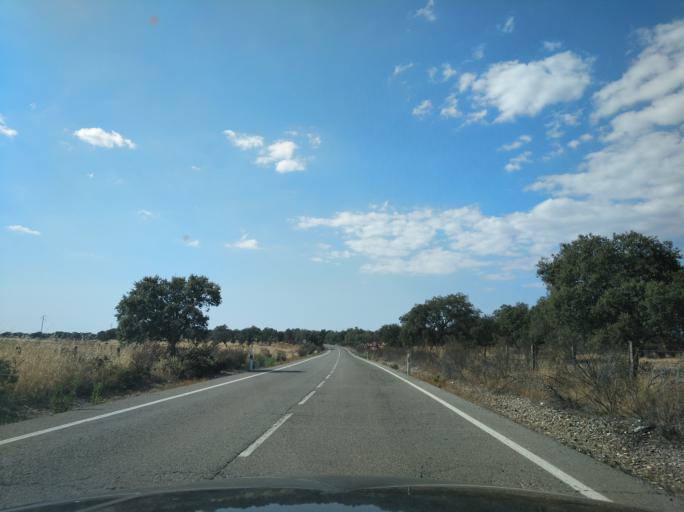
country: ES
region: Andalusia
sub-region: Provincia de Huelva
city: Santa Barbara de Casa
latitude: 37.7652
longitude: -7.1376
